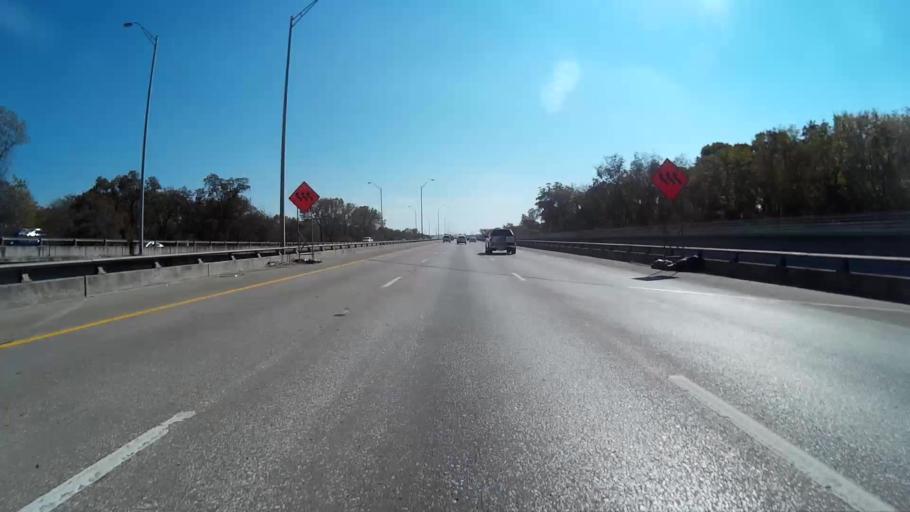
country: US
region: Texas
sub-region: Dallas County
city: Dallas
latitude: 32.7449
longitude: -96.7686
